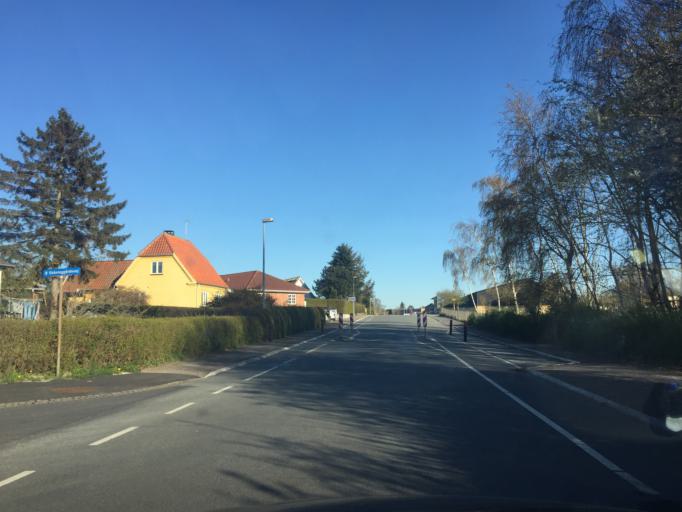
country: DK
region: Capital Region
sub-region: Halsnaes Kommune
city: Frederiksvaerk
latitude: 55.9506
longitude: 12.0312
